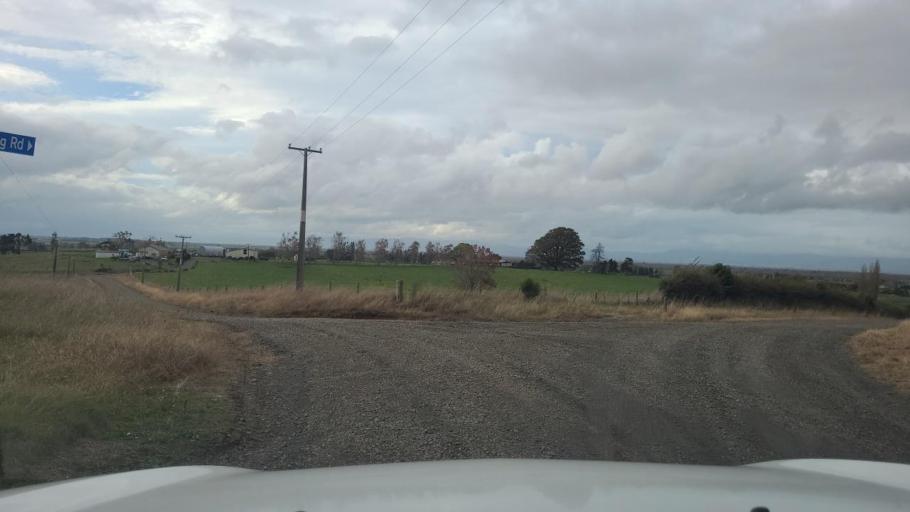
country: NZ
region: Waikato
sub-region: Hauraki District
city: Ngatea
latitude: -37.4348
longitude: 175.4786
